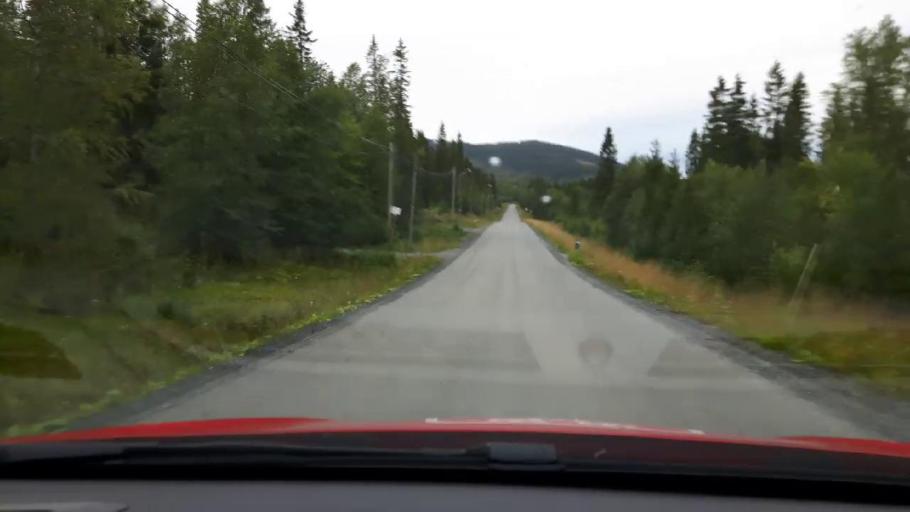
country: SE
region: Jaemtland
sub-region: Are Kommun
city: Are
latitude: 63.4851
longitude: 13.1428
